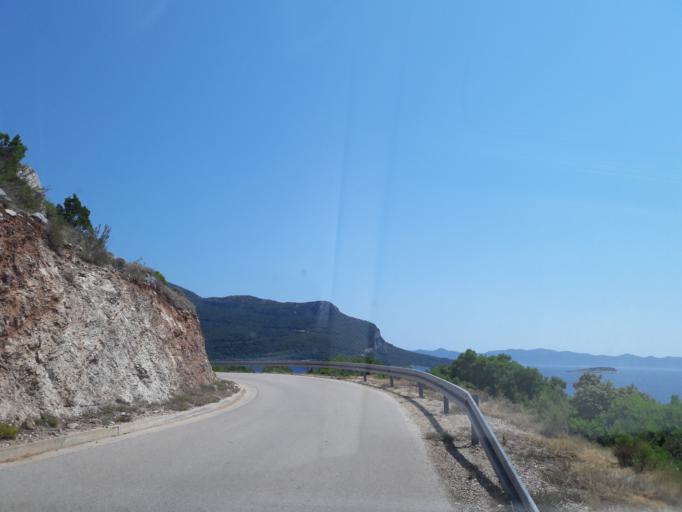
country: HR
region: Dubrovacko-Neretvanska
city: Blato
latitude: 42.9012
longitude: 17.4329
